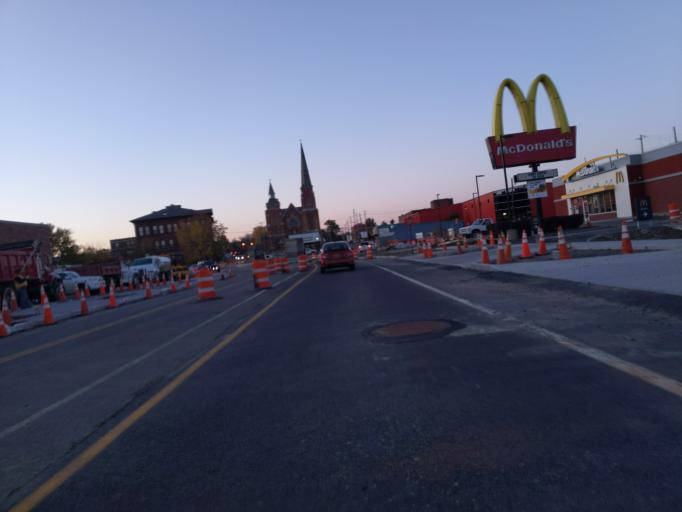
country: US
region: New York
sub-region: Chemung County
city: Elmira
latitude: 42.0920
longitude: -76.8094
